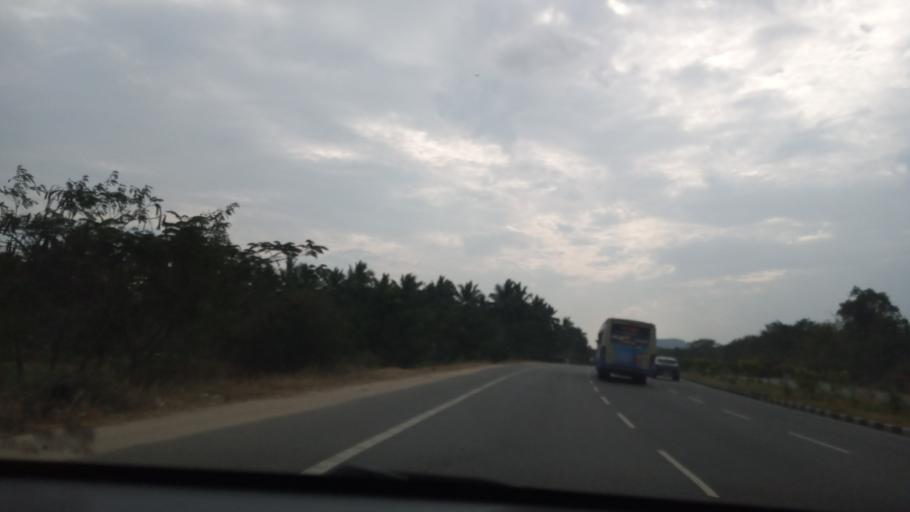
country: IN
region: Tamil Nadu
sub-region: Vellore
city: Jolarpettai
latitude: 12.5431
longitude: 78.4216
